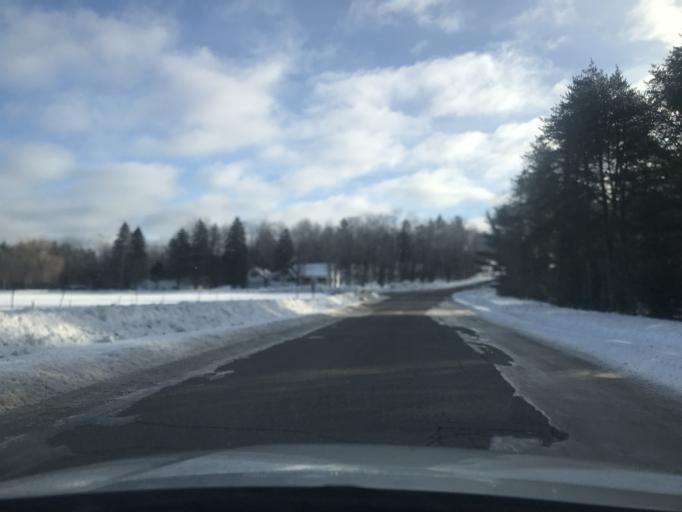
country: US
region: Wisconsin
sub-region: Marinette County
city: Niagara
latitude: 45.6261
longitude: -87.9686
